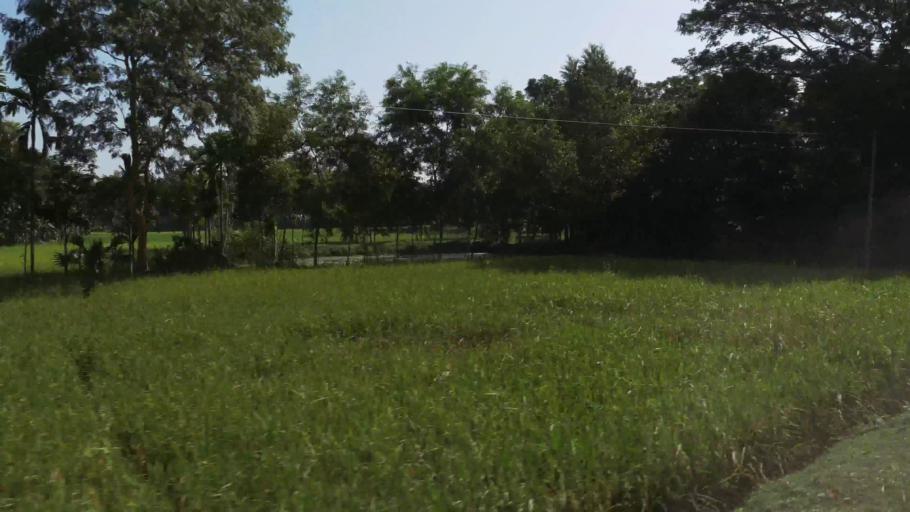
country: BD
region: Dhaka
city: Gafargaon
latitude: 24.5268
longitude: 90.5087
